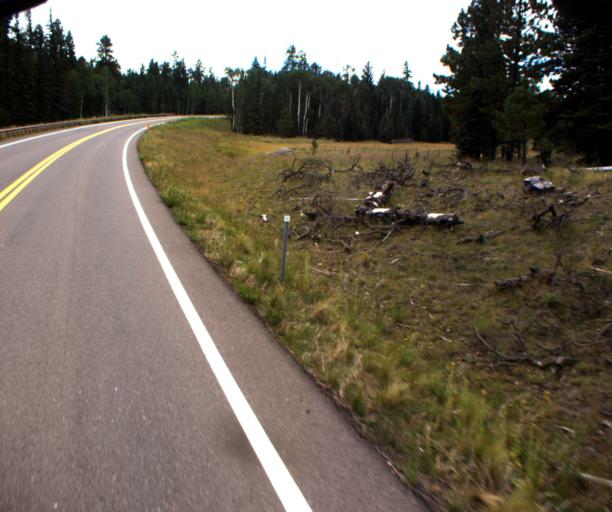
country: US
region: Arizona
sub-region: Apache County
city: Eagar
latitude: 33.9820
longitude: -109.5026
